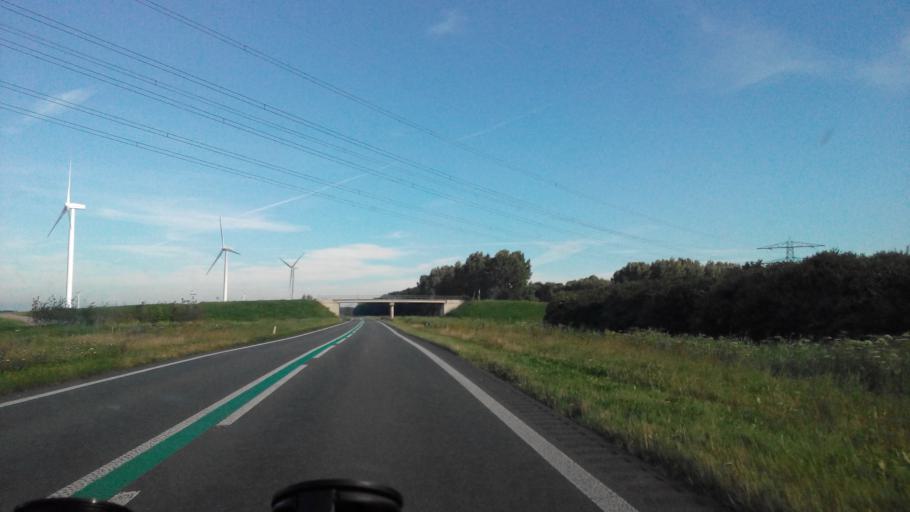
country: NL
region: Utrecht
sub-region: Gemeente Bunschoten
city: Bunschoten
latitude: 52.3097
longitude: 5.4454
